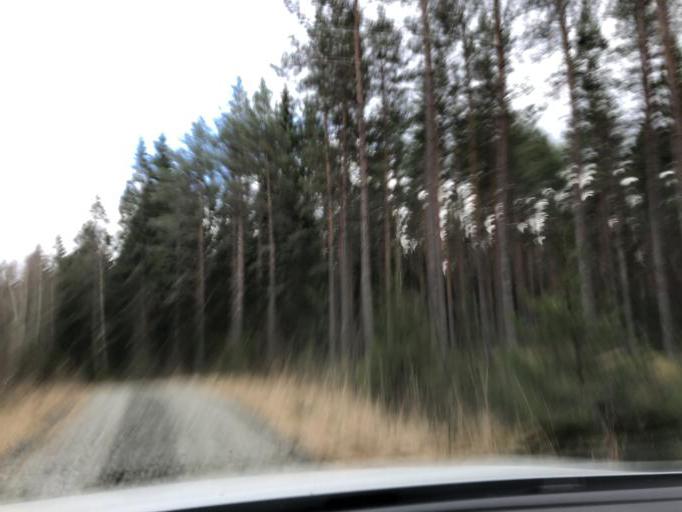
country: SE
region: Uppsala
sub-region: Heby Kommun
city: OEstervala
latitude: 60.3325
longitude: 17.1724
